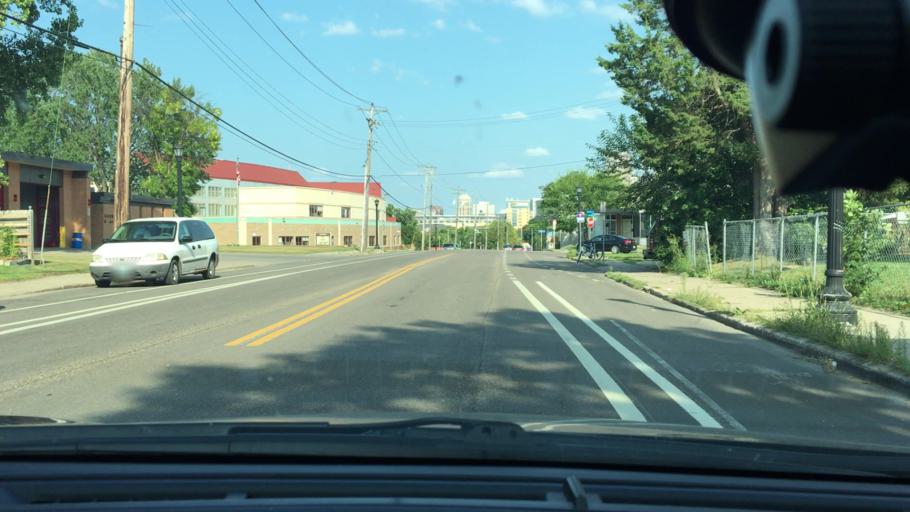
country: US
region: Minnesota
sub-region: Hennepin County
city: Minneapolis
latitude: 44.9809
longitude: -93.3017
